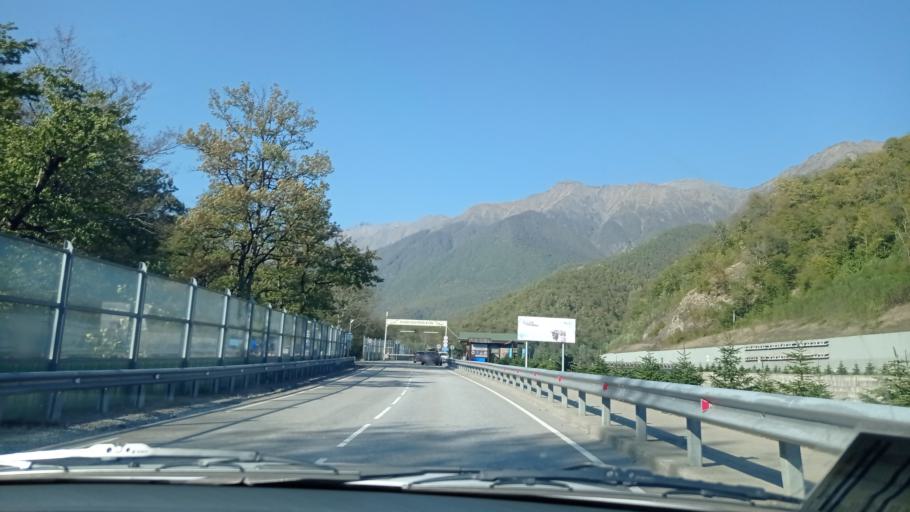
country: RU
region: Krasnodarskiy
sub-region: Sochi City
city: Krasnaya Polyana
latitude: 43.6965
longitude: 40.2692
